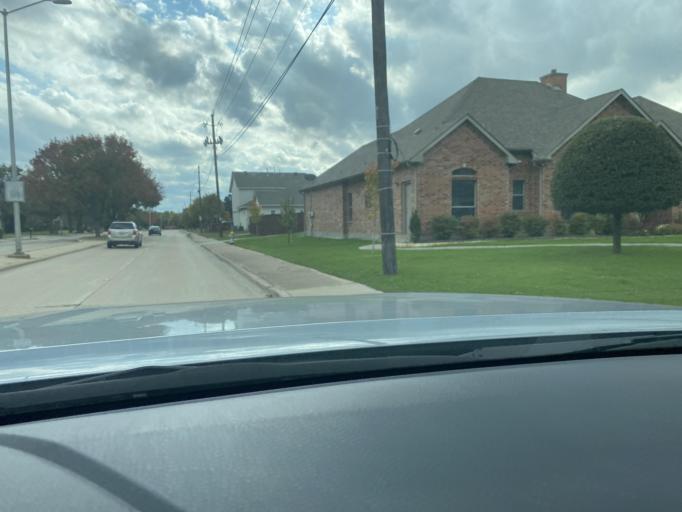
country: US
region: Texas
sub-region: Dallas County
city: Addison
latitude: 32.9938
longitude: -96.7847
